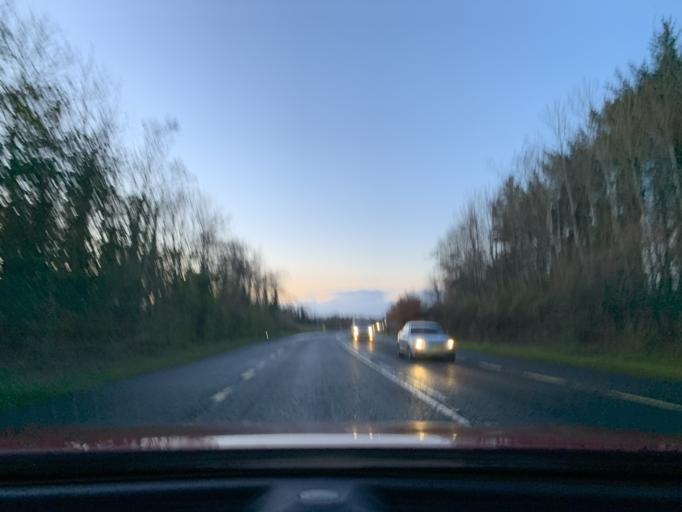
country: IE
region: Connaught
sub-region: County Leitrim
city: Carrick-on-Shannon
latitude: 53.9364
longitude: -8.0544
